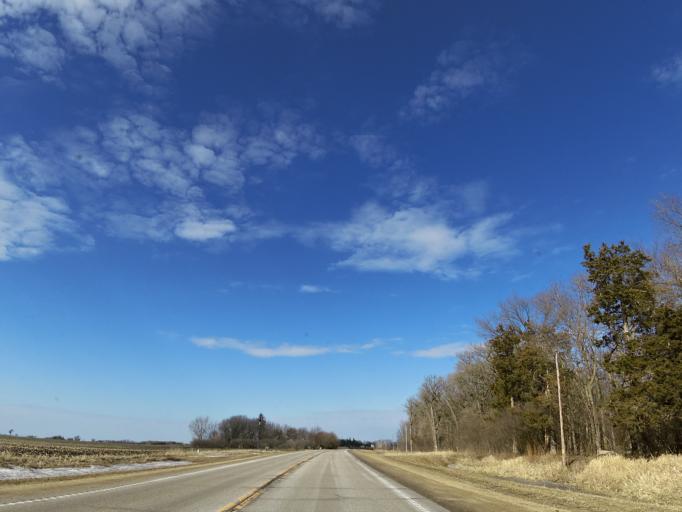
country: US
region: Minnesota
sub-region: Waseca County
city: Waseca
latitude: 44.1253
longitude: -93.5072
